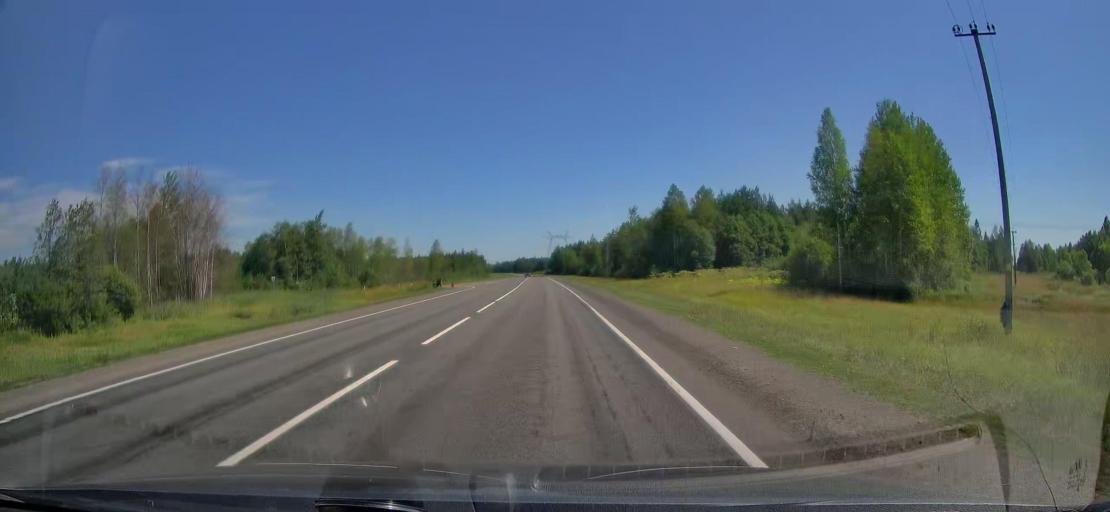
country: RU
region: Tverskaya
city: Ves'yegonsk
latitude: 58.9218
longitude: 37.2179
